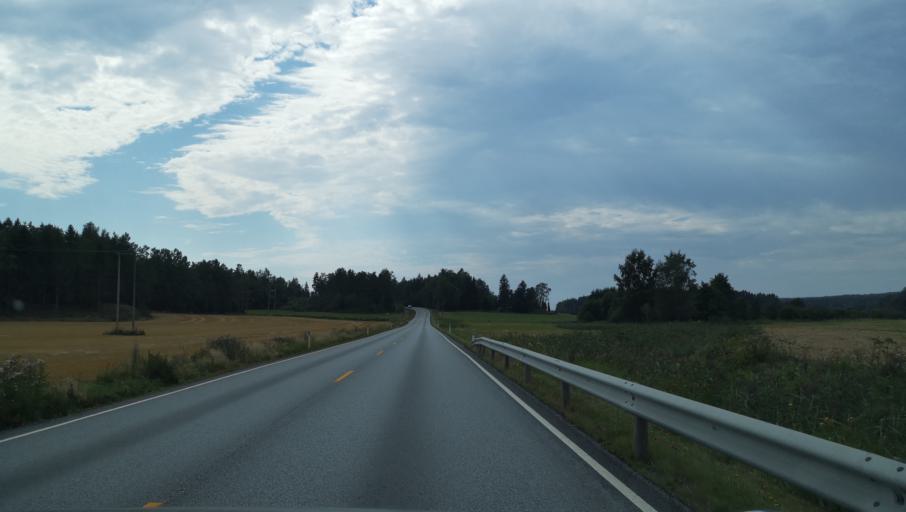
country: NO
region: Ostfold
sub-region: Valer
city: Kirkebygda
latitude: 59.4749
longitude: 10.7885
